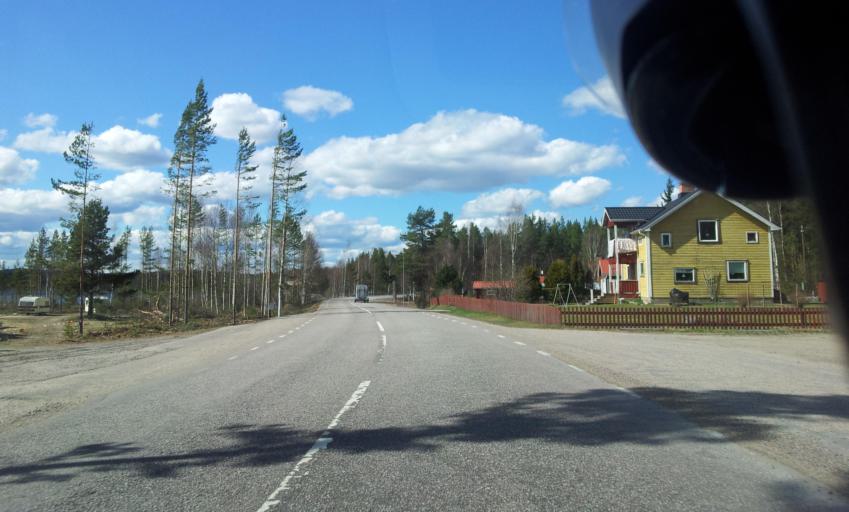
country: SE
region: Gaevleborg
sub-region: Ovanakers Kommun
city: Edsbyn
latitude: 61.2519
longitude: 15.8926
